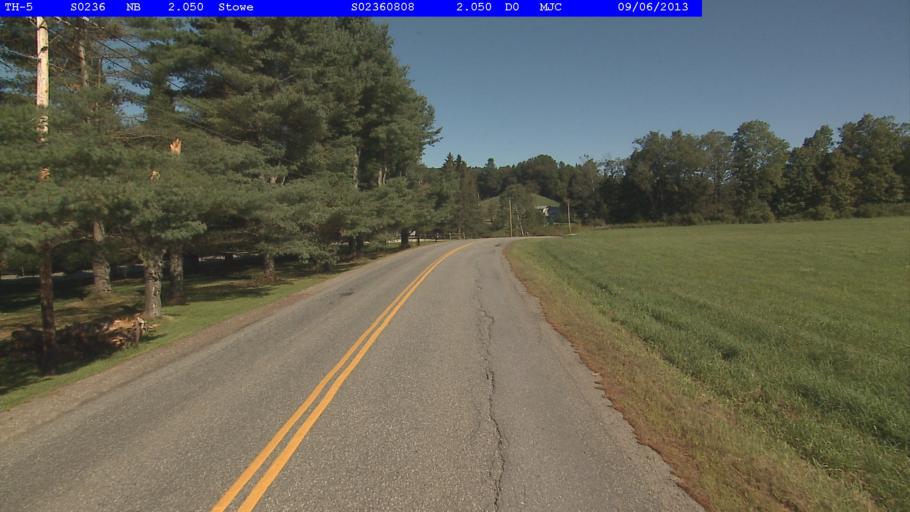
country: US
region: Vermont
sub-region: Washington County
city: Waterbury
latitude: 44.4545
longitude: -72.7295
